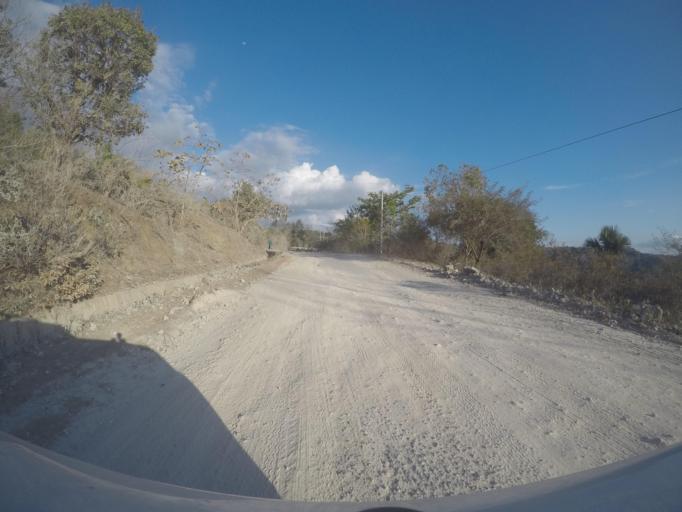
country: ID
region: East Nusa Tenggara
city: Atambua
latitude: -8.9626
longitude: 125.0258
